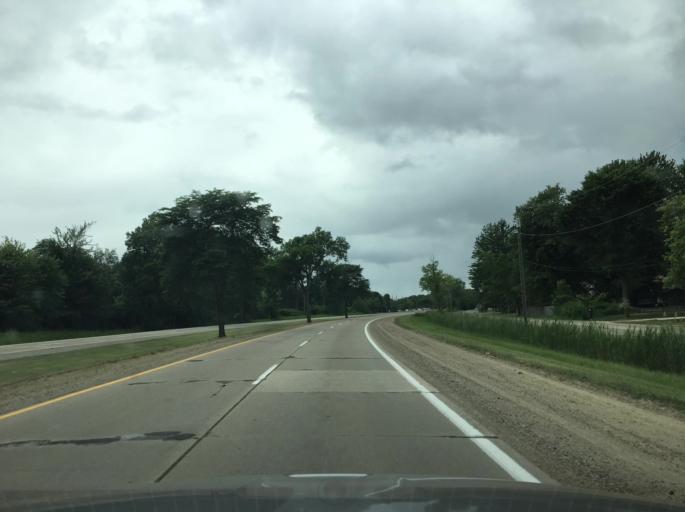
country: US
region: Michigan
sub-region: Macomb County
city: Mount Clemens
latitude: 42.5740
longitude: -82.8379
